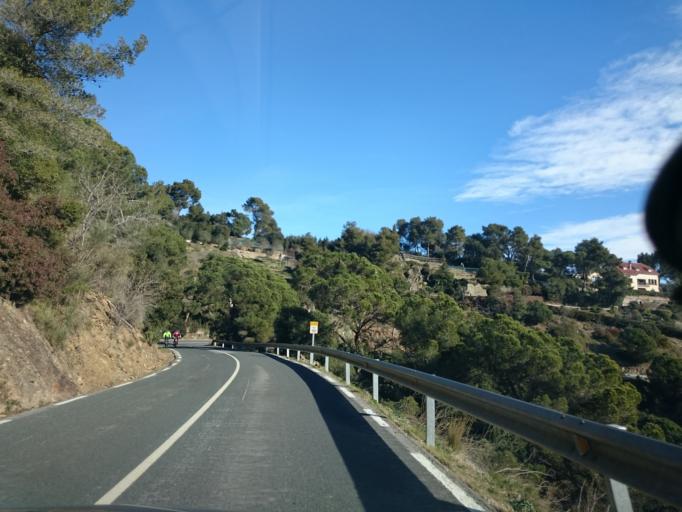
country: ES
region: Catalonia
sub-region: Provincia de Barcelona
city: Sant Just Desvern
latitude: 41.4080
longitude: 2.0860
